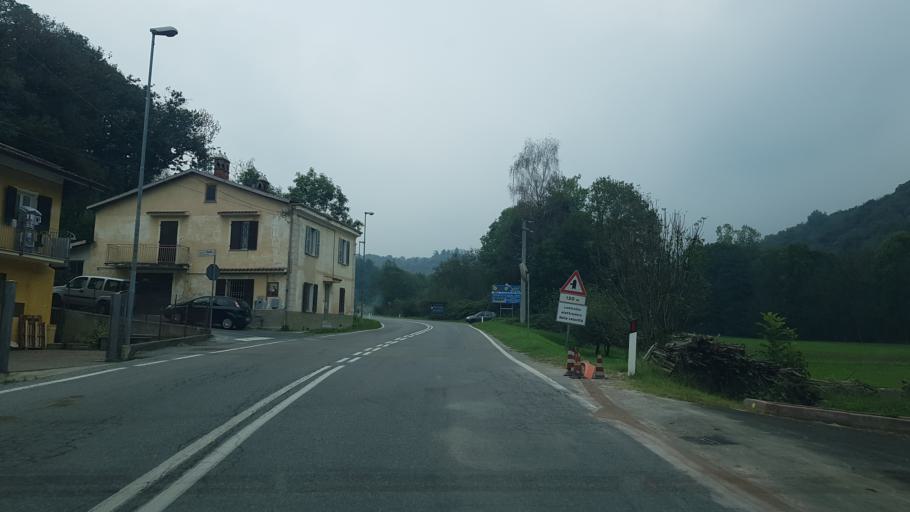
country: IT
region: Piedmont
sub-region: Provincia di Cuneo
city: Frabosa Sottana
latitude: 44.3274
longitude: 7.7937
